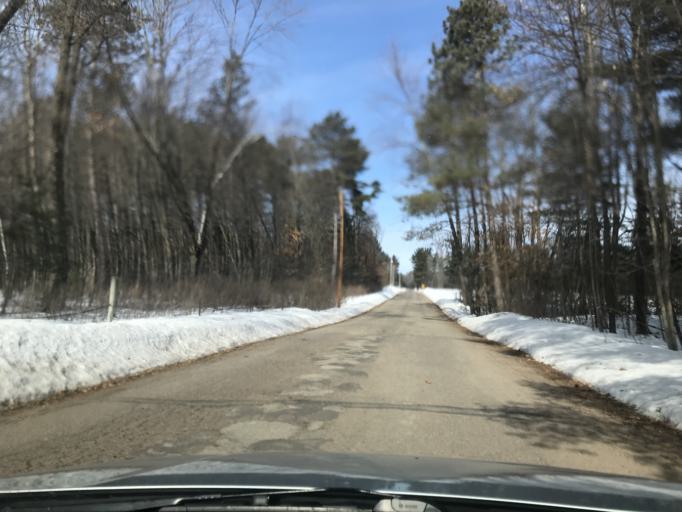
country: US
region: Wisconsin
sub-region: Marinette County
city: Peshtigo
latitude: 45.2229
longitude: -87.9628
